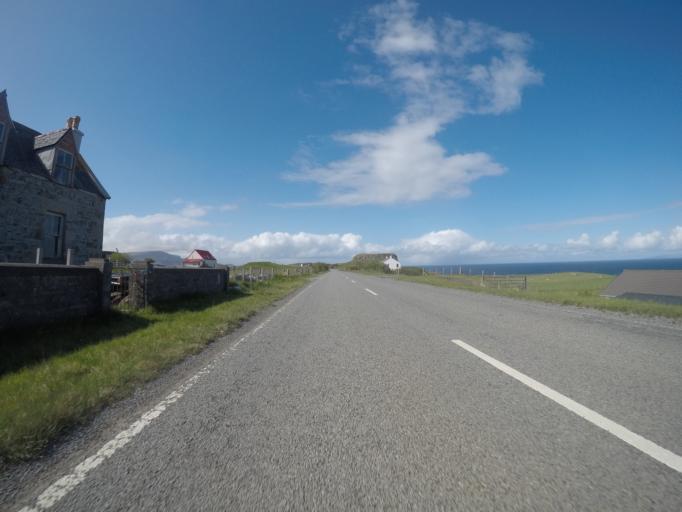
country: GB
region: Scotland
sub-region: Highland
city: Portree
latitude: 57.5962
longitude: -6.1614
